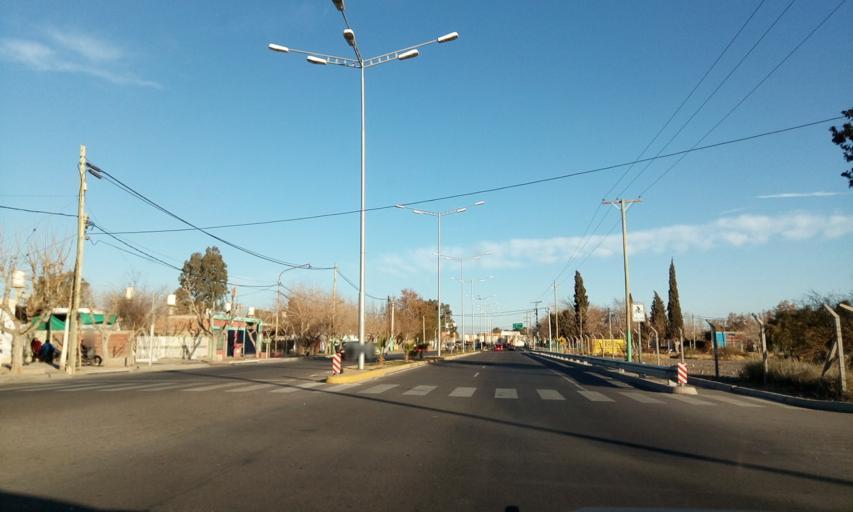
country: AR
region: San Juan
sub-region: Departamento de Rivadavia
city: Rivadavia
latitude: -31.5227
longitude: -68.6280
